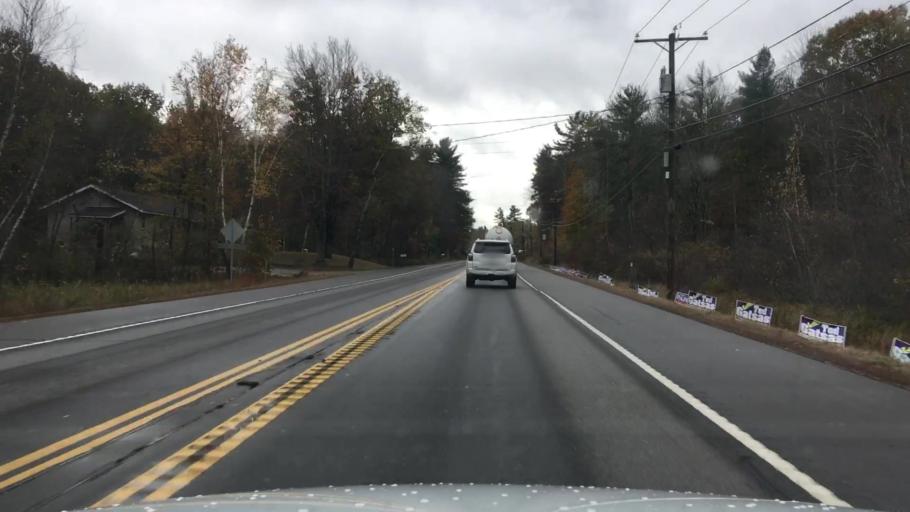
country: US
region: New Hampshire
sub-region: Strafford County
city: Lee
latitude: 43.1409
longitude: -71.0119
